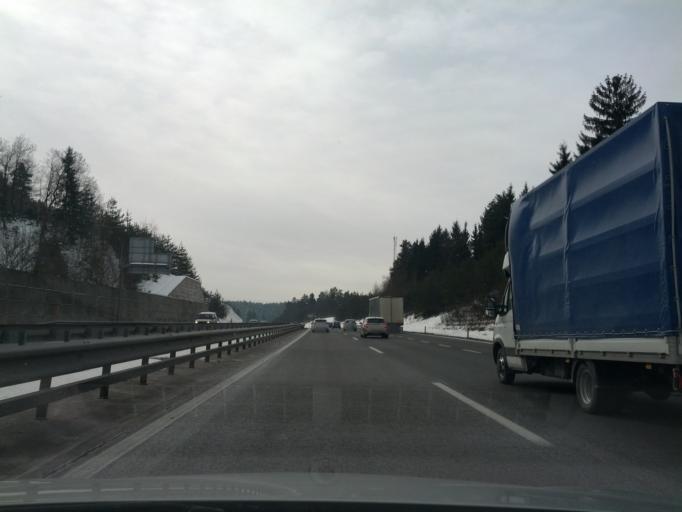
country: SI
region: Skofljica
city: Lavrica
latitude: 46.0372
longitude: 14.5739
